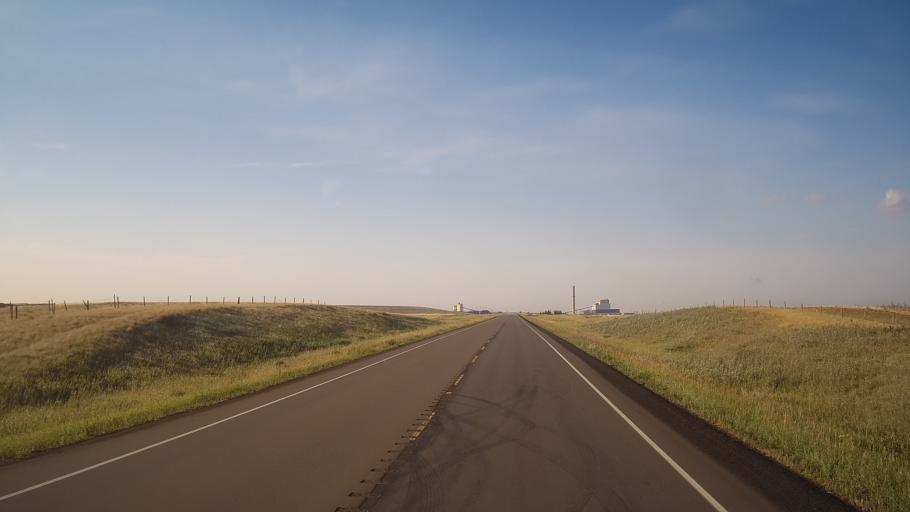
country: CA
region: Alberta
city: Hanna
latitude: 51.4736
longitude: -111.7868
